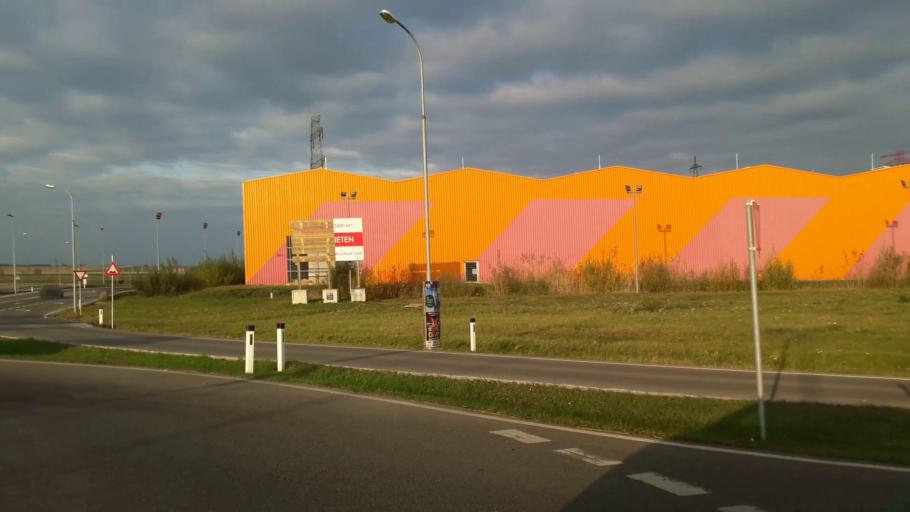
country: AT
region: Lower Austria
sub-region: Politischer Bezirk Mistelbach
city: Grossebersdorf
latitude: 48.3439
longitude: 16.4651
